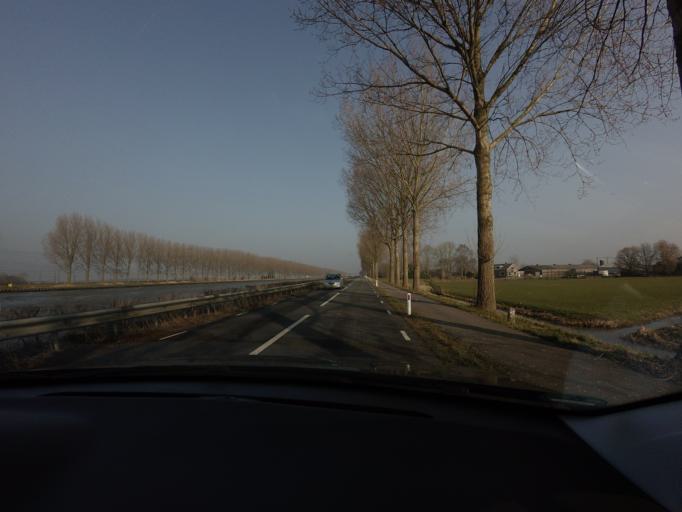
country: NL
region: Utrecht
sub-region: Stichtse Vecht
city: Vreeland
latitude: 52.2370
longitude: 5.0104
